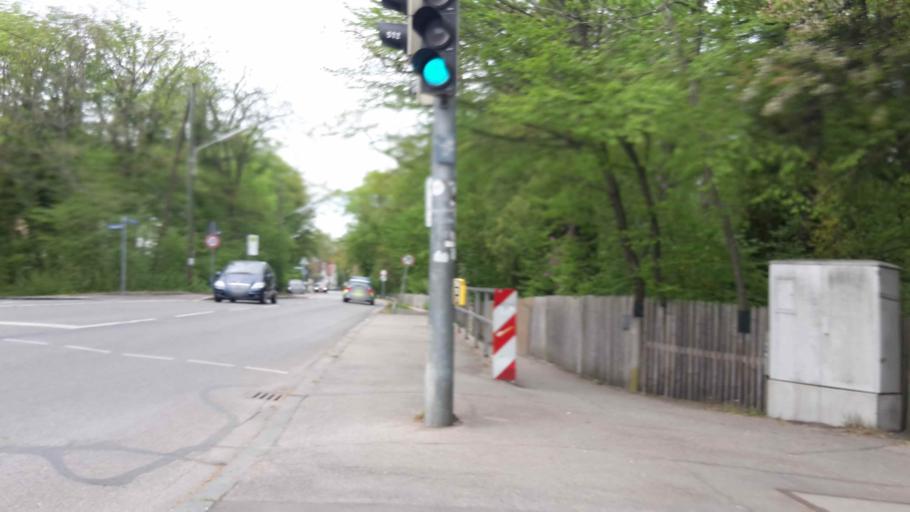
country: DE
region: Bavaria
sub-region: Upper Bavaria
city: Pasing
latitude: 48.1668
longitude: 11.4878
